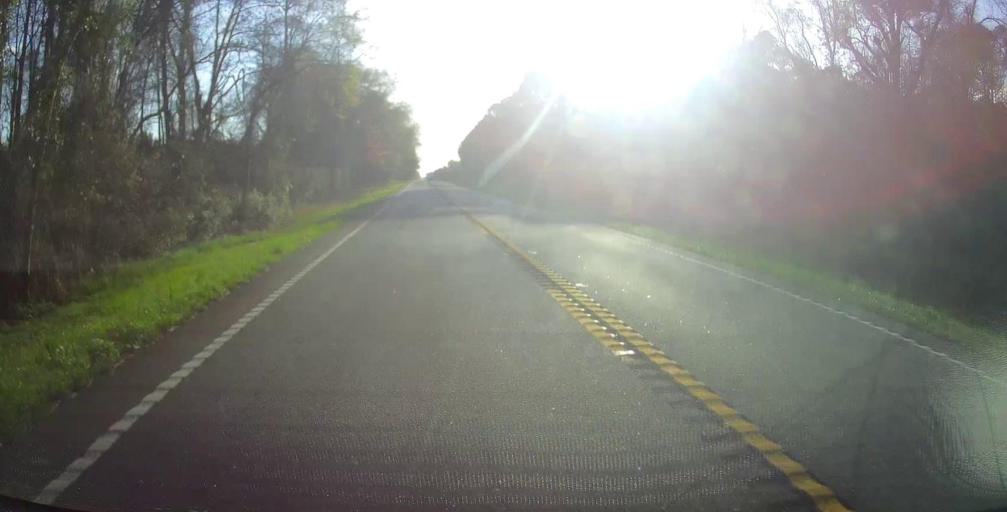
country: US
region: Georgia
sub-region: Tattnall County
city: Reidsville
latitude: 32.1352
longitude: -82.0426
